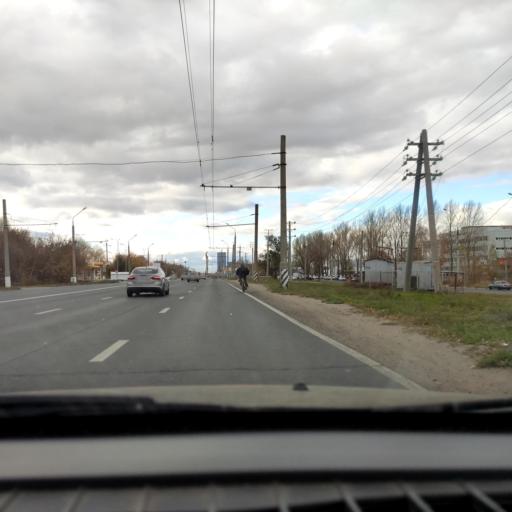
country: RU
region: Samara
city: Tol'yatti
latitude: 53.5525
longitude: 49.2978
